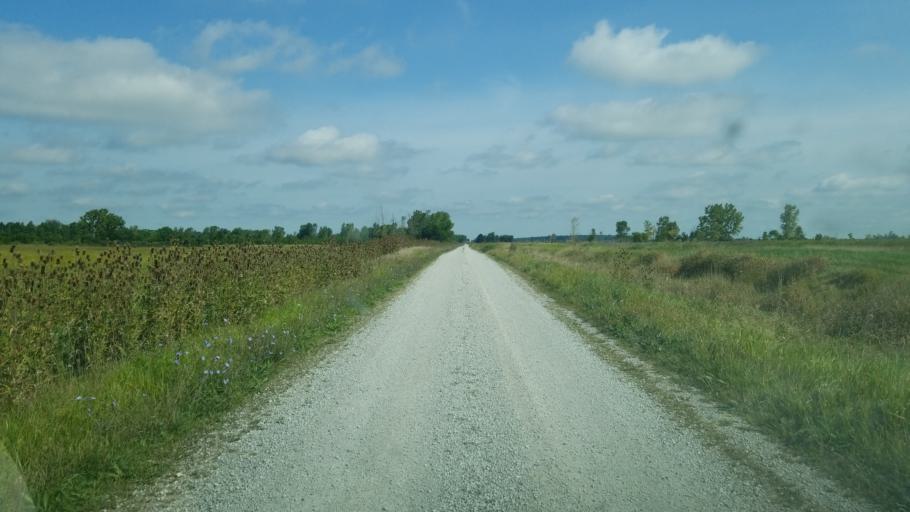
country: US
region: Ohio
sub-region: Wyandot County
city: Upper Sandusky
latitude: 40.7128
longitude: -83.3239
